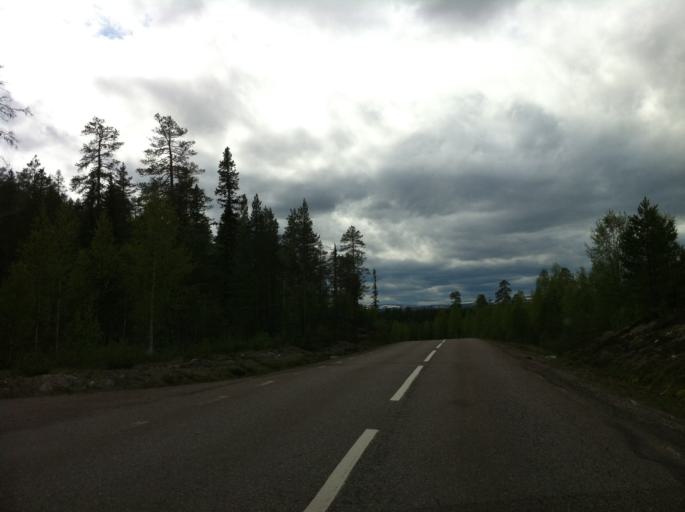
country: NO
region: Hedmark
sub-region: Trysil
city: Innbygda
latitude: 61.5744
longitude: 13.1057
